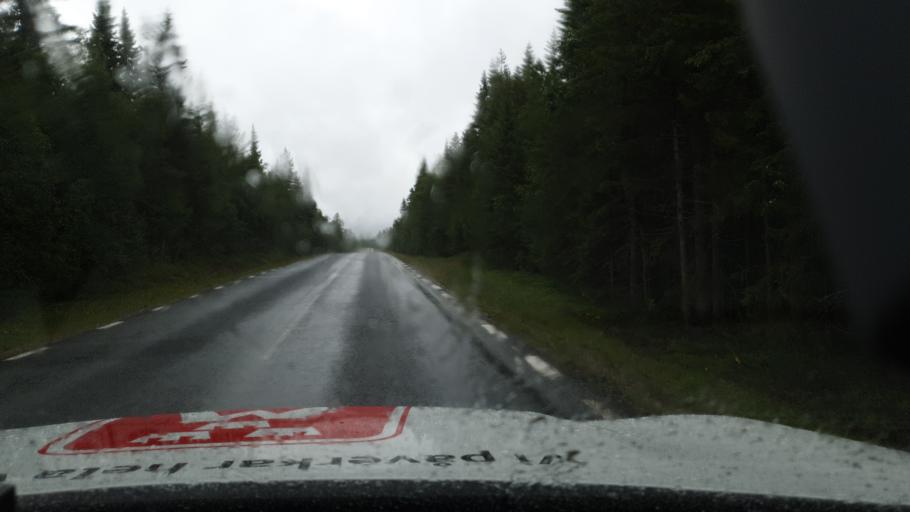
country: SE
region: Vaesterbotten
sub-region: Asele Kommun
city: Insjon
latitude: 64.3583
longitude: 17.9193
